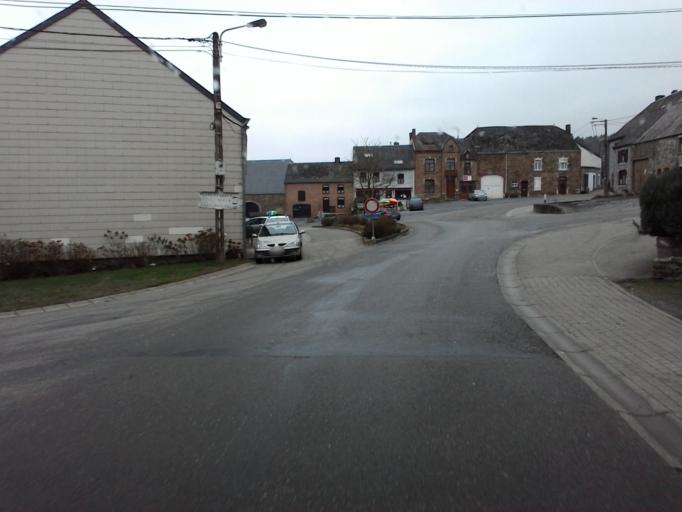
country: BE
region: Wallonia
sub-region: Province de Namur
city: Gedinne
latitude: 50.0322
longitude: 4.9208
